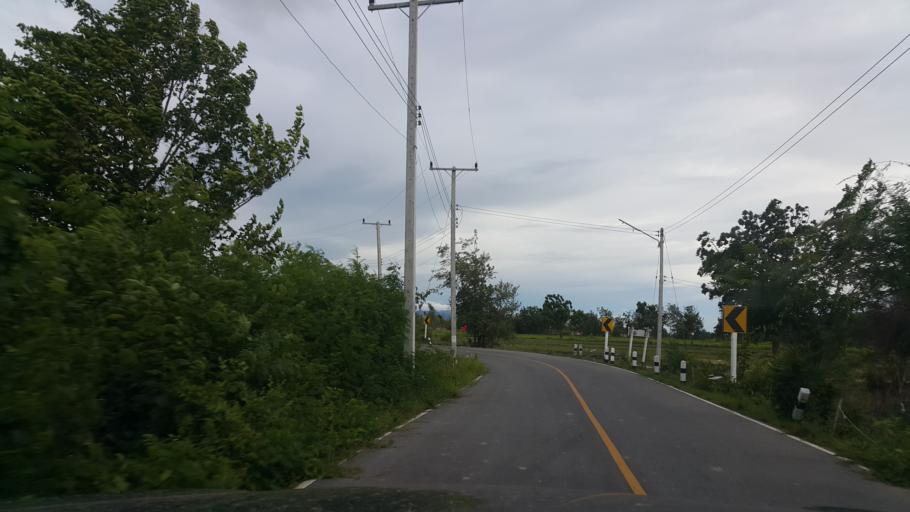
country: TH
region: Sukhothai
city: Ban Dan Lan Hoi
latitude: 17.1601
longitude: 99.5018
